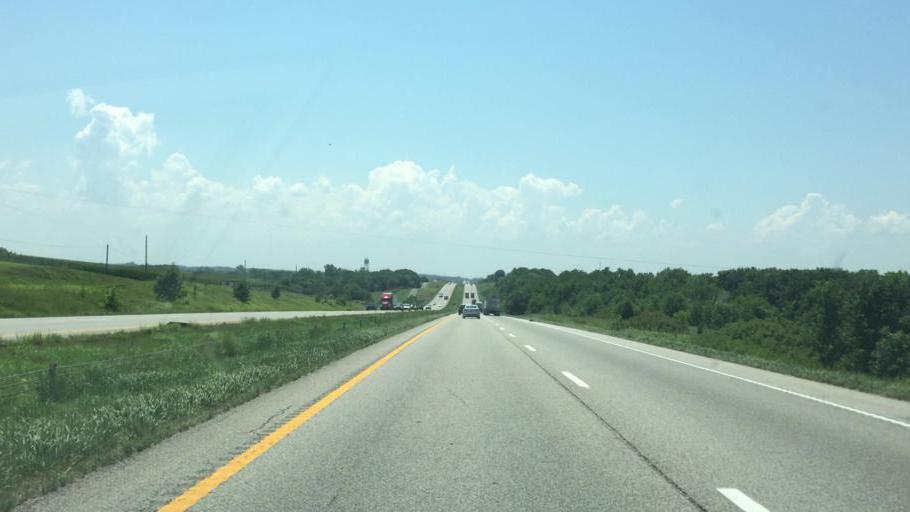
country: US
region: Missouri
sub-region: Platte County
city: Platte City
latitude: 39.5453
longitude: -94.7878
